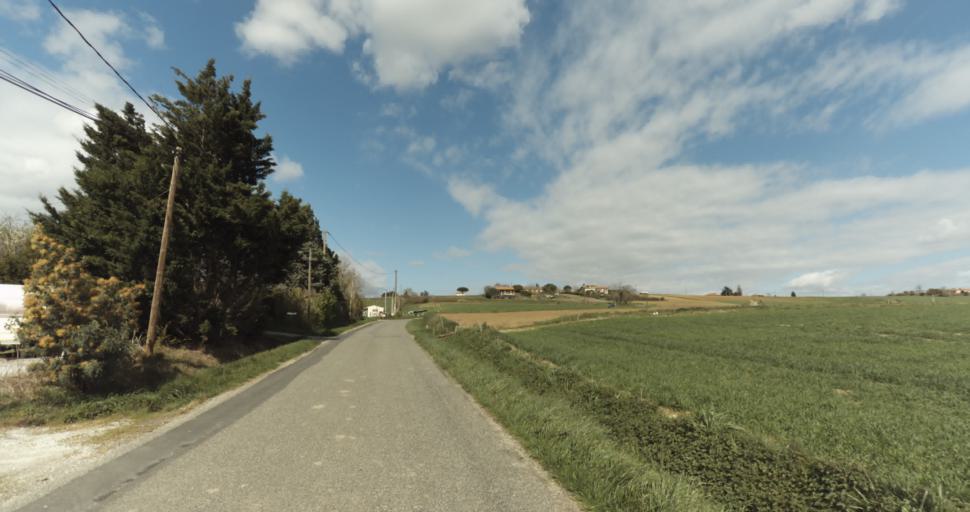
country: FR
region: Midi-Pyrenees
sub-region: Departement de la Haute-Garonne
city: Auterive
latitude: 43.3642
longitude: 1.4823
